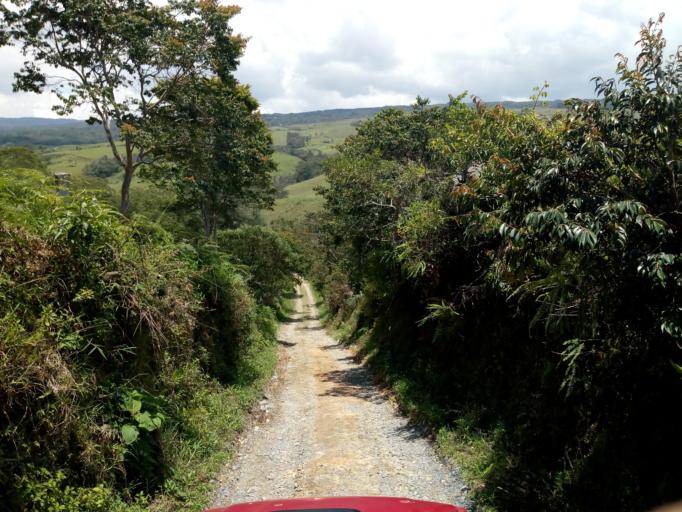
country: CO
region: Boyaca
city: Moniquira
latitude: 5.8672
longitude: -73.5023
